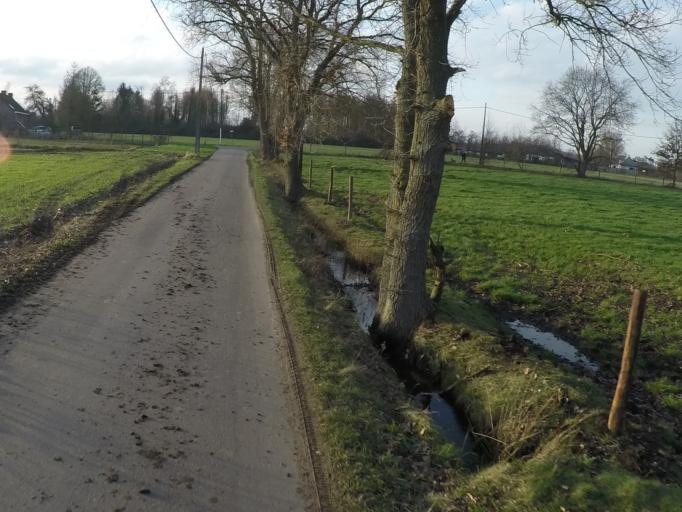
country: BE
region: Flanders
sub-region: Provincie Antwerpen
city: Putte
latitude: 51.0357
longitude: 4.6471
